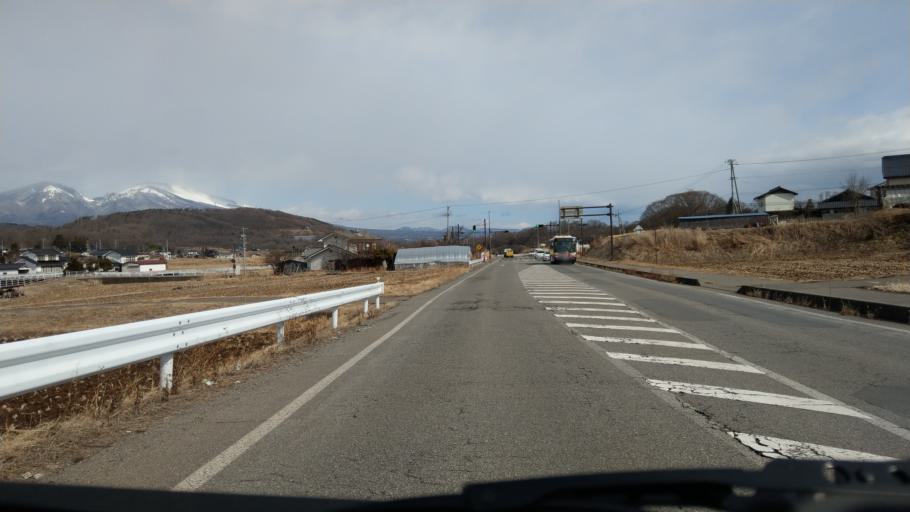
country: JP
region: Nagano
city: Komoro
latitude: 36.2772
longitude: 138.3952
